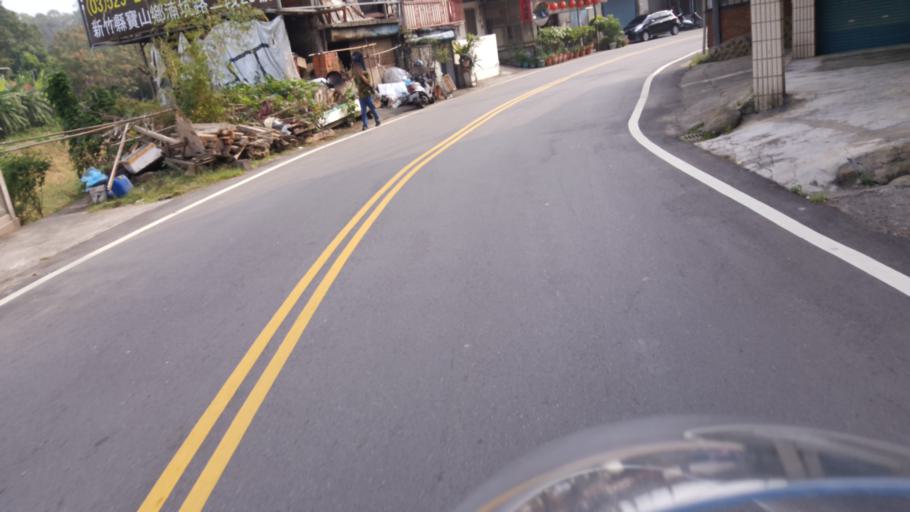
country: TW
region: Taiwan
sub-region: Hsinchu
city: Hsinchu
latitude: 24.7312
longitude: 120.9650
